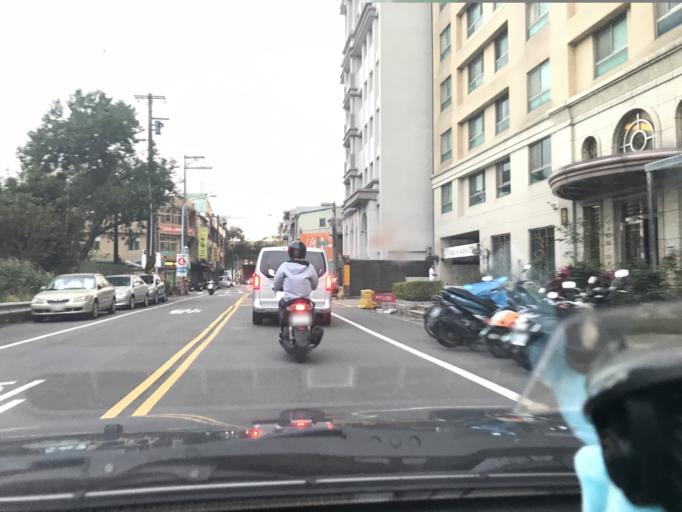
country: TW
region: Taiwan
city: Daxi
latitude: 24.8627
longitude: 121.2194
